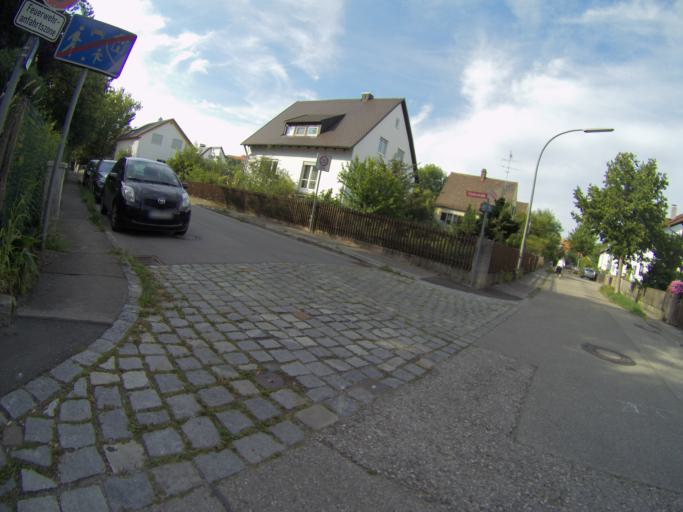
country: DE
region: Bavaria
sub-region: Upper Bavaria
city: Freising
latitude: 48.3891
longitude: 11.7325
